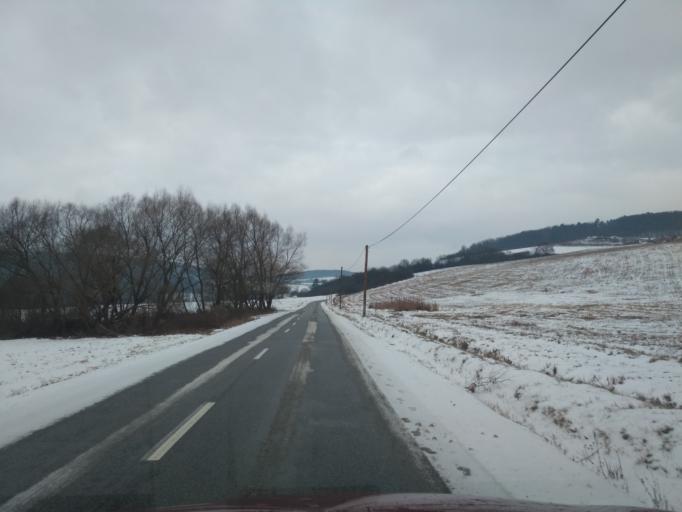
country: SK
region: Presovsky
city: Sabinov
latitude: 49.0214
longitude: 21.1118
